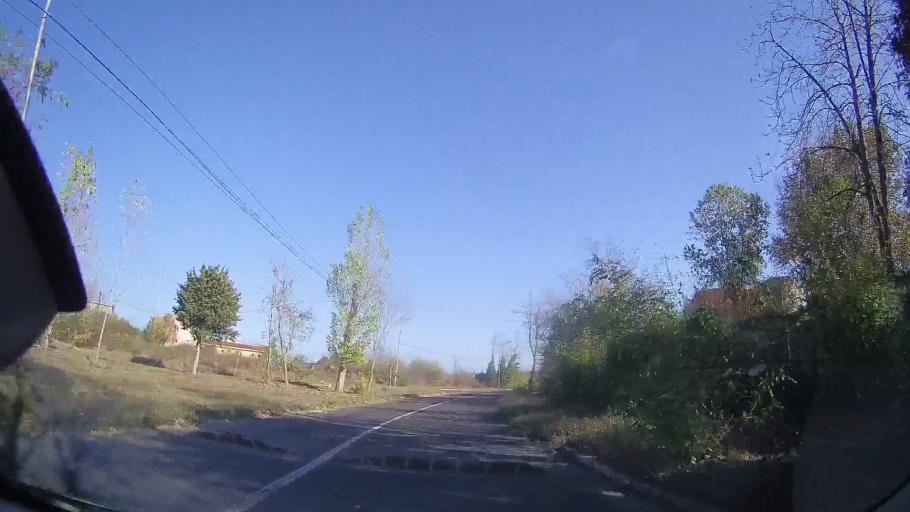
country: RO
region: Constanta
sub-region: Municipiul Mangalia
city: Mangalia
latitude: 43.8480
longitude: 28.5915
